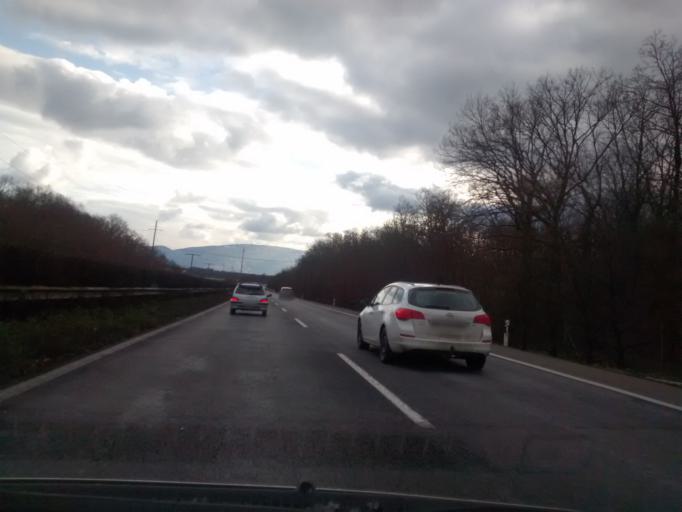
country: CH
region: Geneva
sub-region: Geneva
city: Versoix
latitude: 46.3030
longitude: 6.1442
